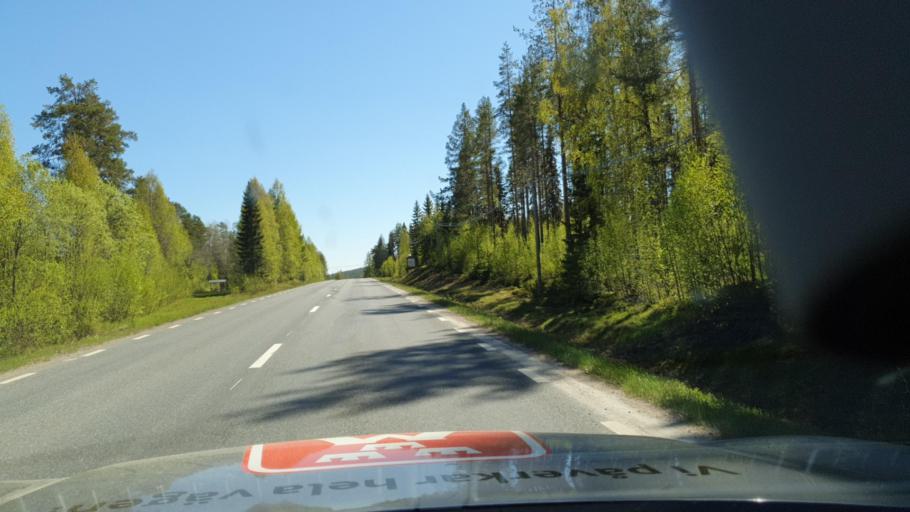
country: SE
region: Vaesternorrland
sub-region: OErnskoeldsviks Kommun
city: Ornskoldsvik
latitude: 63.6627
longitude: 18.5393
